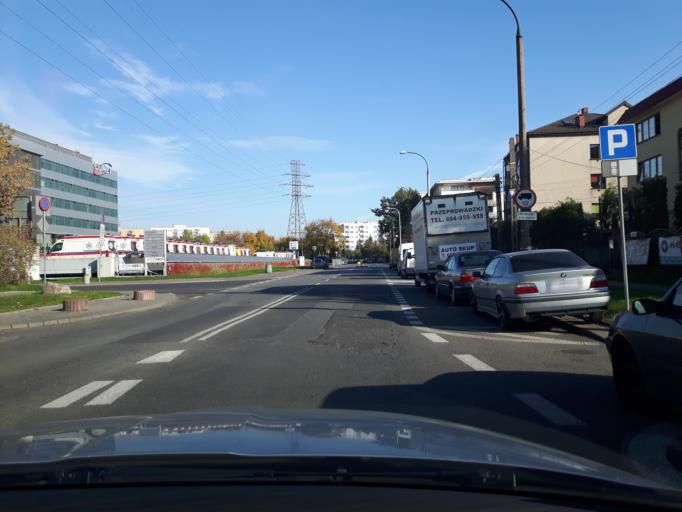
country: PL
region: Masovian Voivodeship
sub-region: Warszawa
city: Bemowo
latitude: 52.2339
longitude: 20.9273
